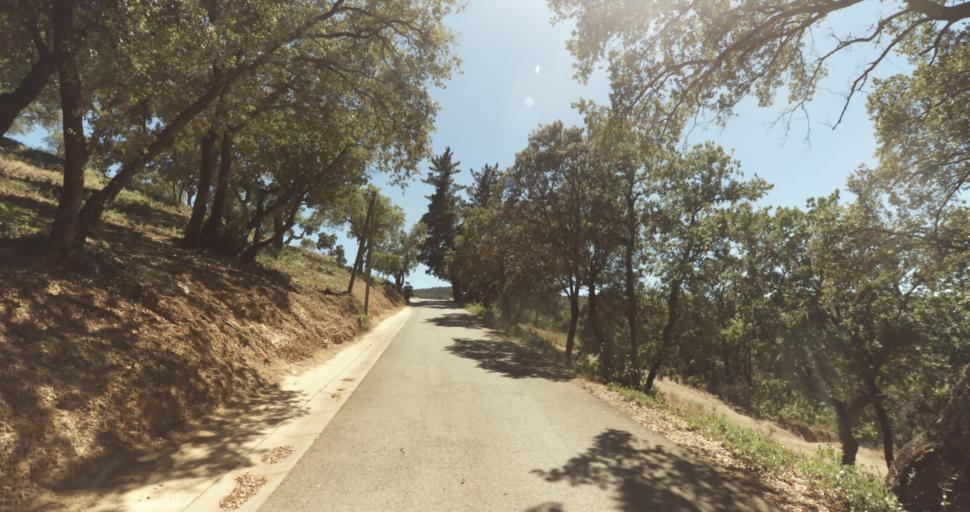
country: FR
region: Provence-Alpes-Cote d'Azur
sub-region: Departement du Var
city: La Croix-Valmer
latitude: 43.2262
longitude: 6.5596
